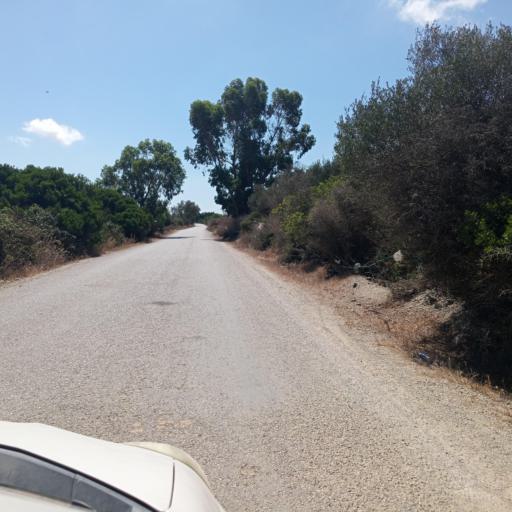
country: TN
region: Nabul
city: Qulaybiyah
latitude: 36.8622
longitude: 11.0398
